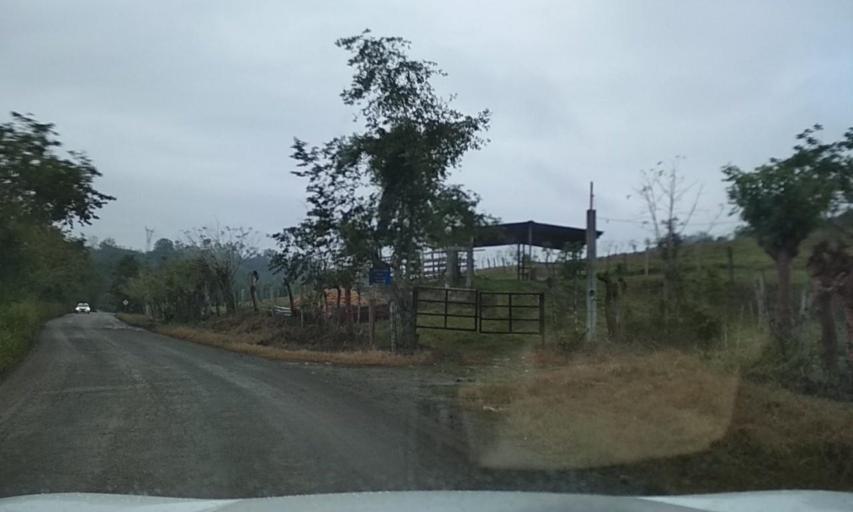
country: MX
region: Veracruz
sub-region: Coatzintla
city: Manuel Maria Contreras
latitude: 20.4628
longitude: -97.4728
